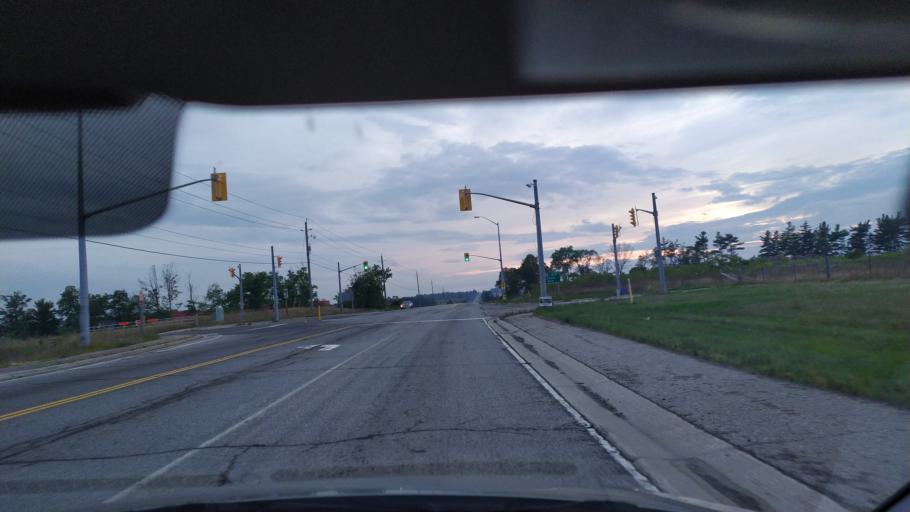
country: CA
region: Ontario
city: Kitchener
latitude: 43.3306
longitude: -80.4528
